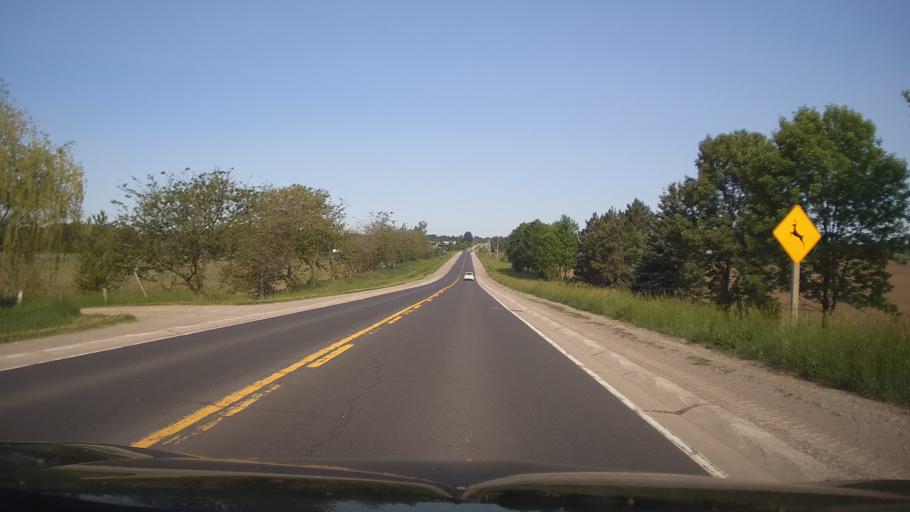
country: CA
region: Ontario
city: Omemee
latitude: 44.2952
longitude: -78.5971
